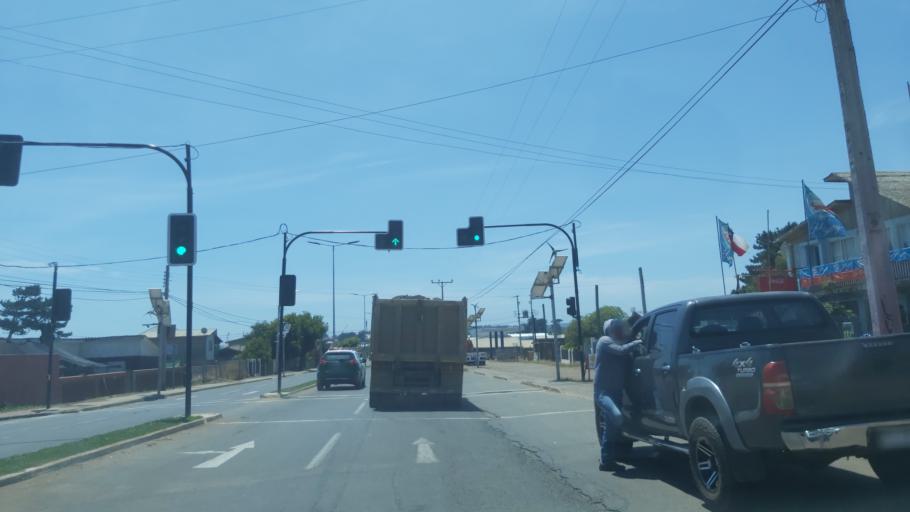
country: CL
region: Maule
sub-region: Provincia de Cauquenes
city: Cauquenes
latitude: -35.8113
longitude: -72.5721
